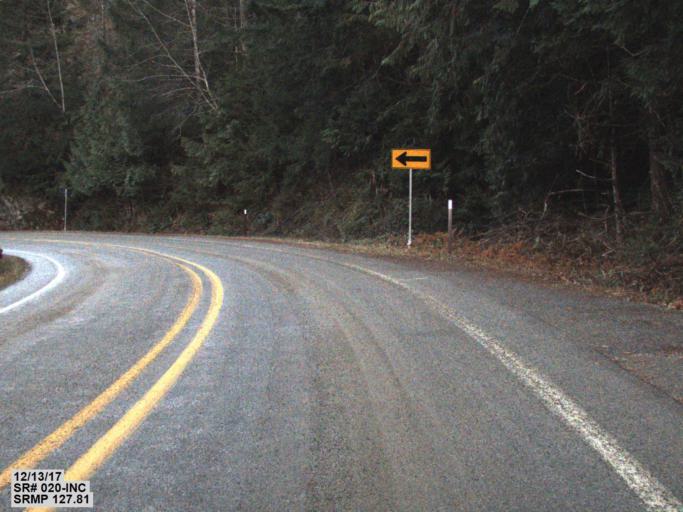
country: US
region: Washington
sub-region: Snohomish County
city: Darrington
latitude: 48.7105
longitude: -121.1294
